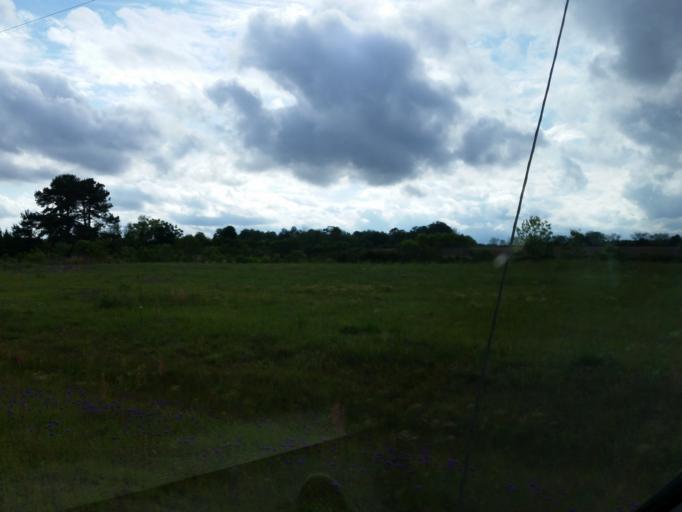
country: US
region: Georgia
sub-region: Dooly County
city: Unadilla
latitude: 32.2096
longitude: -83.7499
